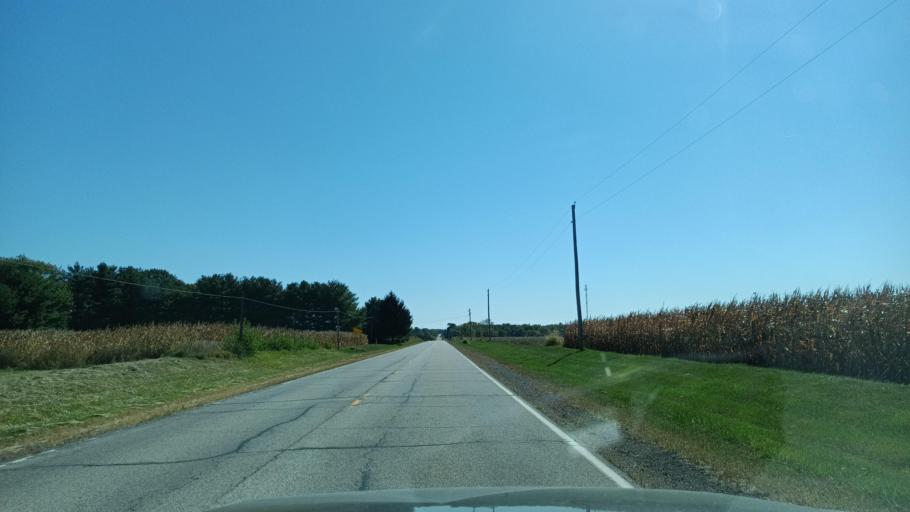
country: US
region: Illinois
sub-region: Peoria County
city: Elmwood
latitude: 40.8513
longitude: -89.9185
